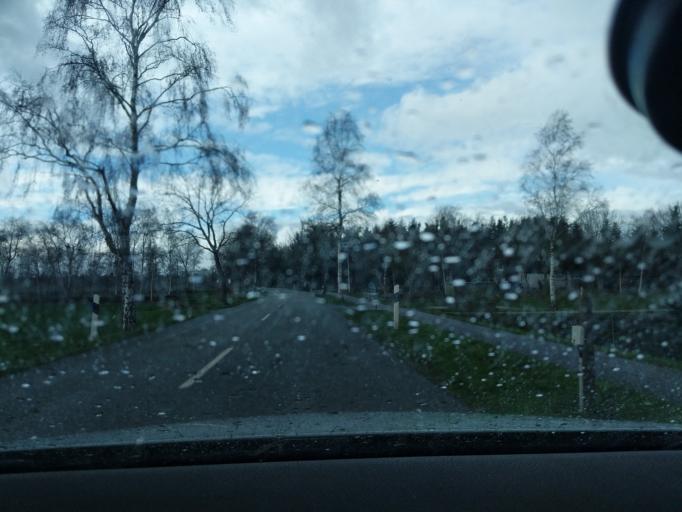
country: DE
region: Lower Saxony
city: Drochtersen
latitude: 53.6609
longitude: 9.4169
